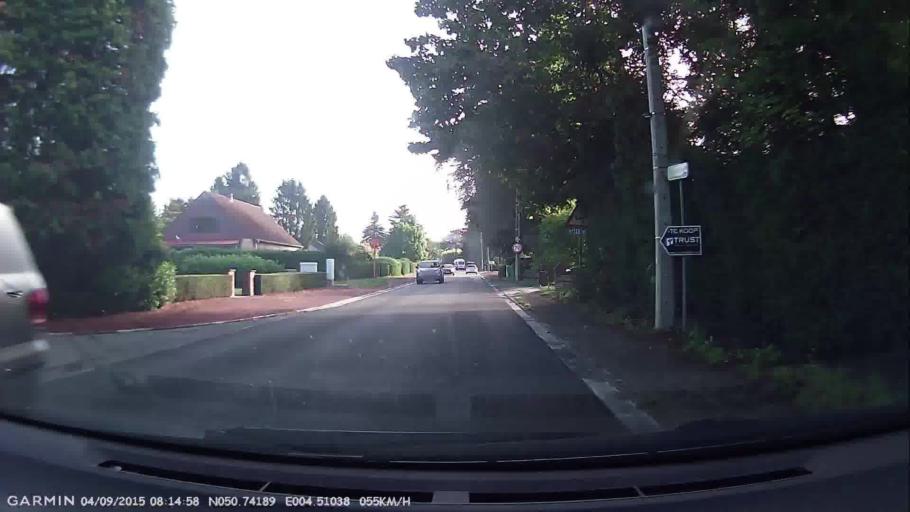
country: BE
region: Wallonia
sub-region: Province du Brabant Wallon
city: La Hulpe
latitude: 50.7421
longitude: 4.5107
